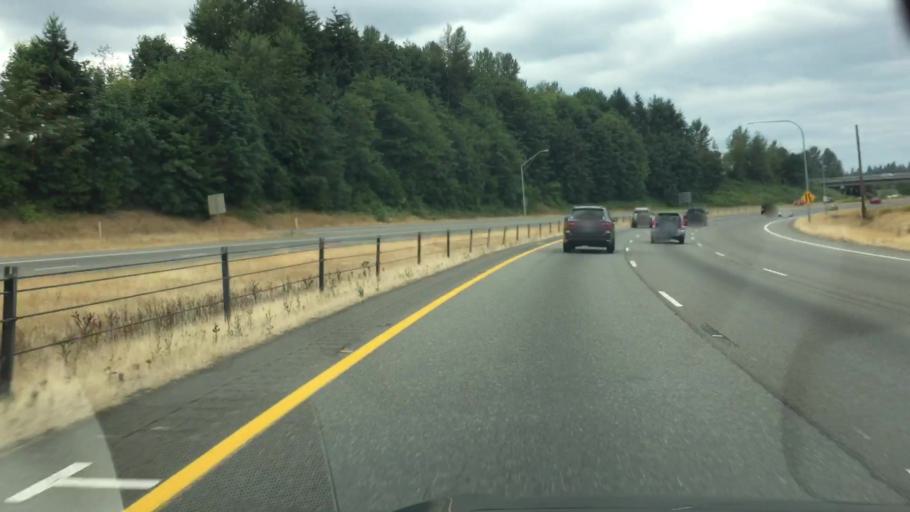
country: US
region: Washington
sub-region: Pierce County
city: Puyallup
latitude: 47.1599
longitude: -122.2992
